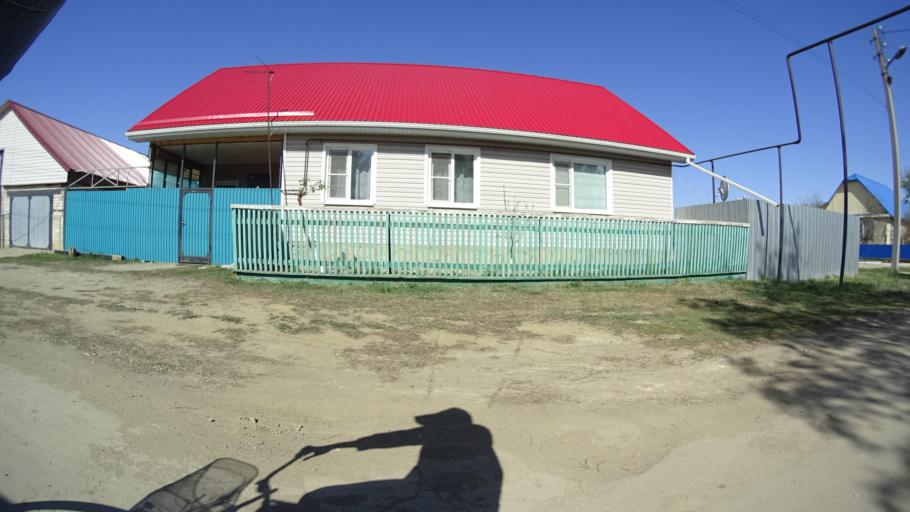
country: RU
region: Chelyabinsk
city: Chesma
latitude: 53.7930
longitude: 61.0341
